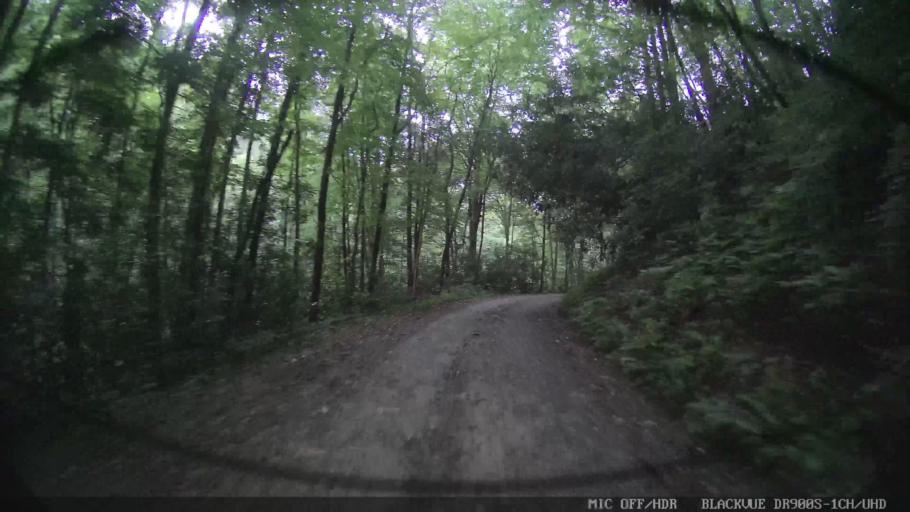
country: US
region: Georgia
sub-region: Gilmer County
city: Ellijay
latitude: 34.8149
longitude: -84.5650
